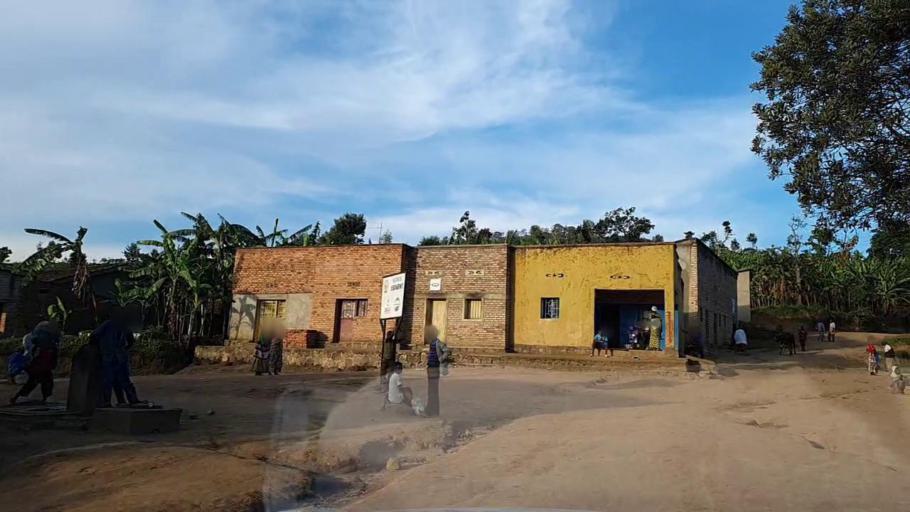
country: RW
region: Southern Province
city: Gikongoro
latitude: -2.3966
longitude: 29.5542
